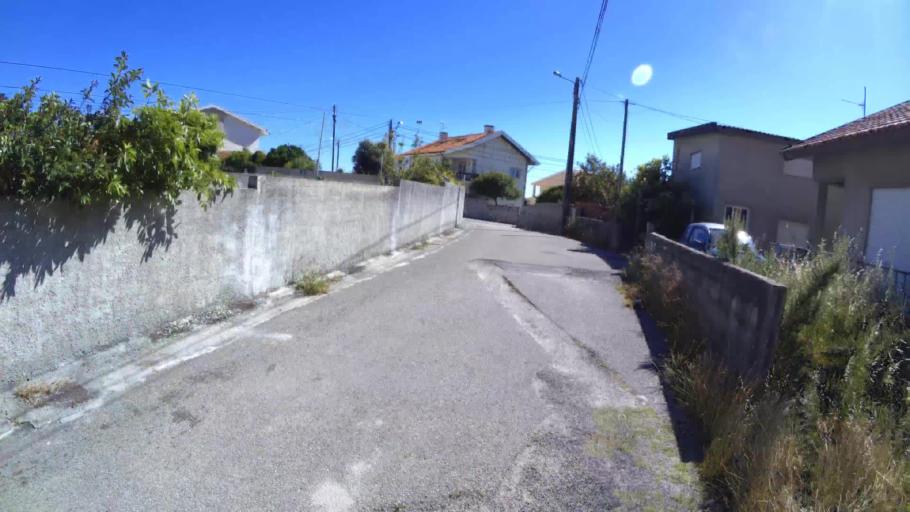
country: PT
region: Aveiro
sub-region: Aveiro
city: Aveiro
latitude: 40.6638
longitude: -8.6228
